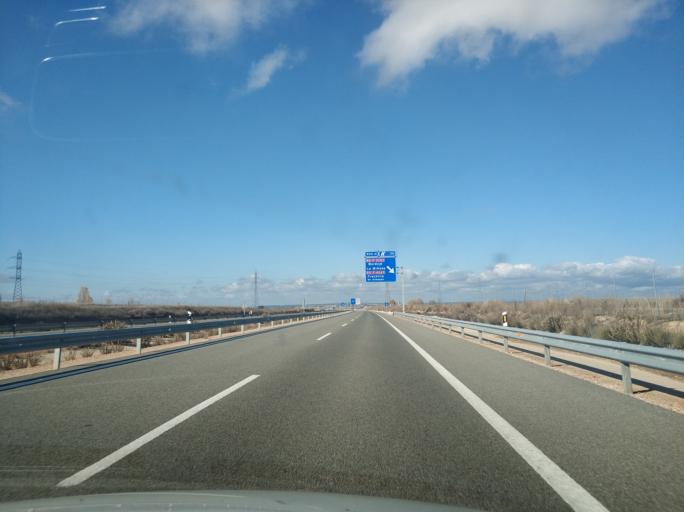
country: ES
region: Castille and Leon
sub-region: Provincia de Soria
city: Frechilla de Almazan
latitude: 41.4383
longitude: -2.5001
